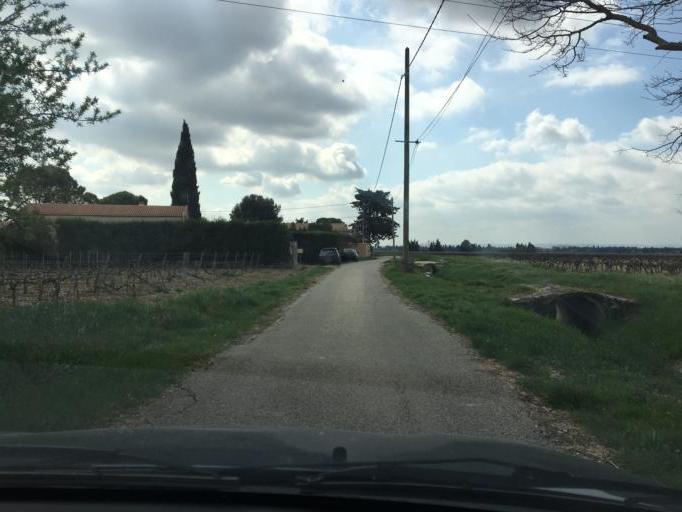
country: FR
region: Provence-Alpes-Cote d'Azur
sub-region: Departement du Vaucluse
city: Serignan-du-Comtat
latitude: 44.1801
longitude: 4.8342
